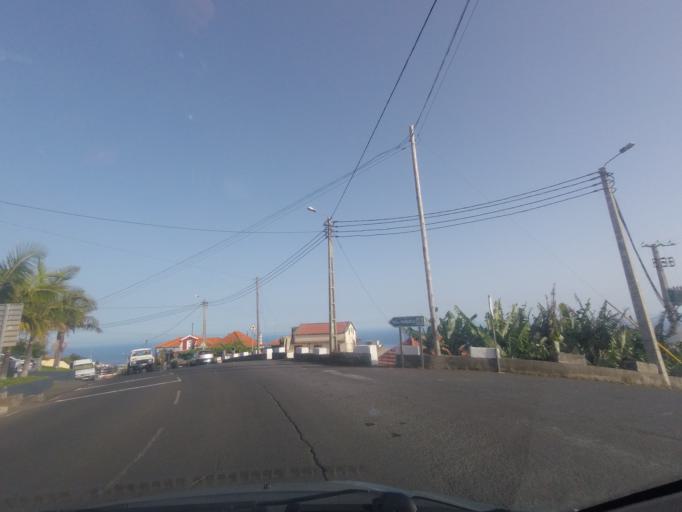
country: PT
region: Madeira
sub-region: Calheta
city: Arco da Calheta
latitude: 32.7006
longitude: -17.1246
